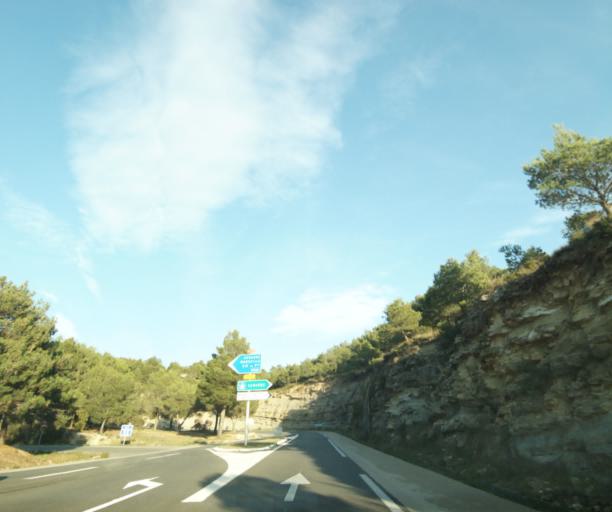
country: FR
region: Provence-Alpes-Cote d'Azur
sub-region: Departement des Bouches-du-Rhone
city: Roquefort-la-Bedoule
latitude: 43.2261
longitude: 5.5851
